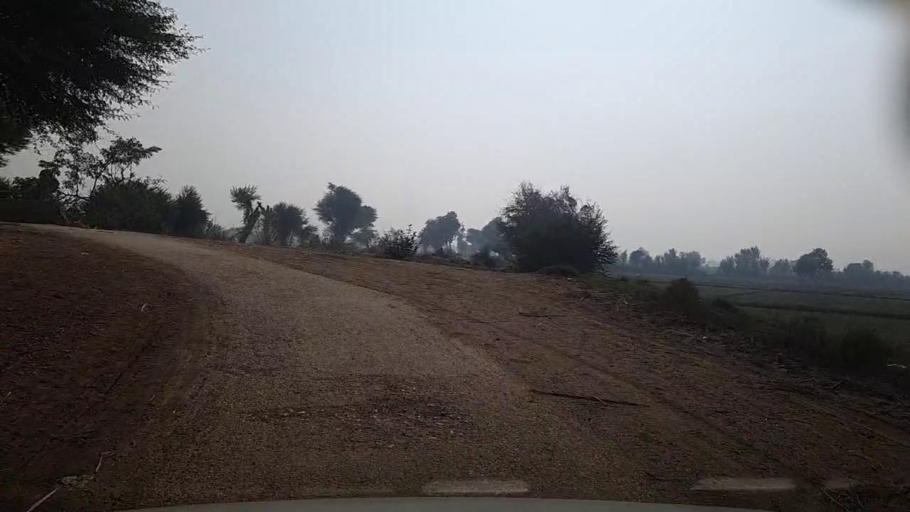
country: PK
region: Sindh
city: Setharja Old
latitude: 27.1312
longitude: 68.5118
